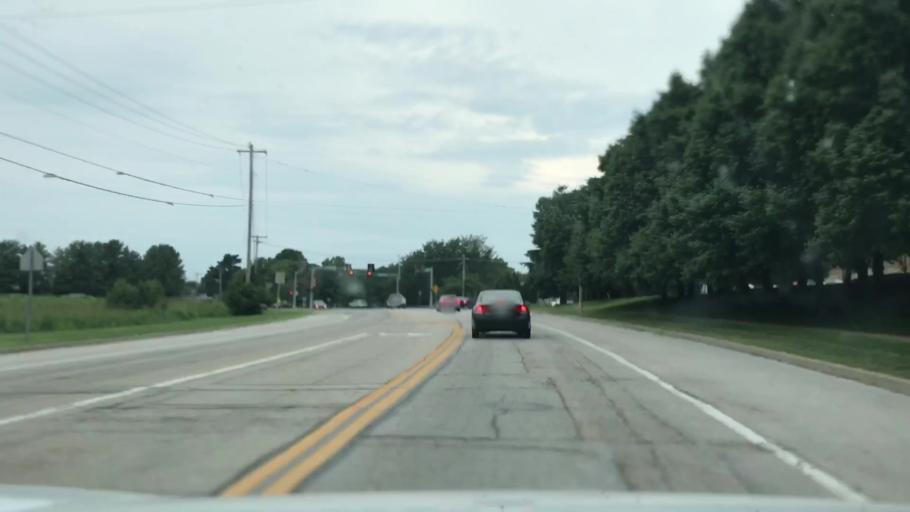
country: US
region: Missouri
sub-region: Saint Louis County
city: Chesterfield
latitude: 38.6603
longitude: -90.5800
